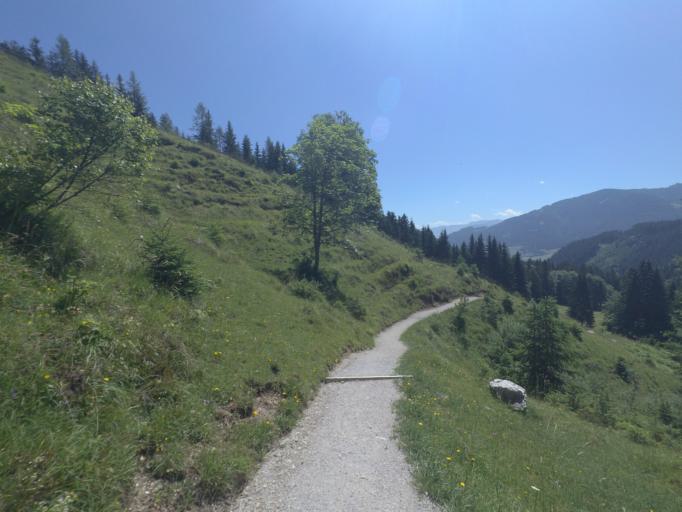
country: AT
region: Salzburg
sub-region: Politischer Bezirk Zell am See
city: Leogang
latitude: 47.4565
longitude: 12.7531
